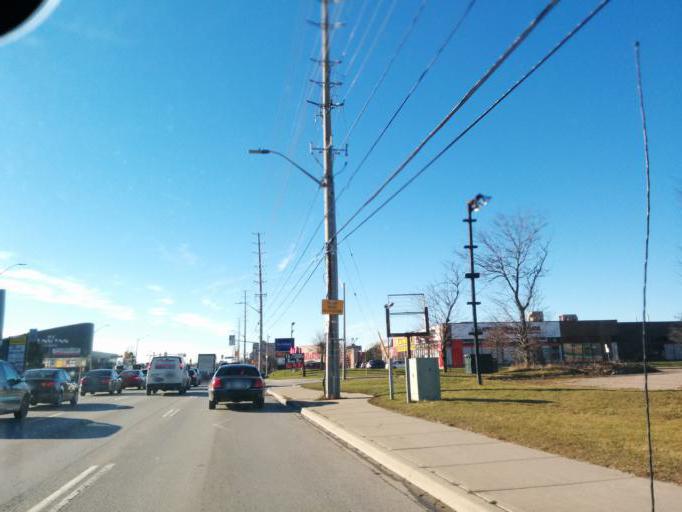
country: CA
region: Ontario
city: Etobicoke
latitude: 43.6156
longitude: -79.5771
